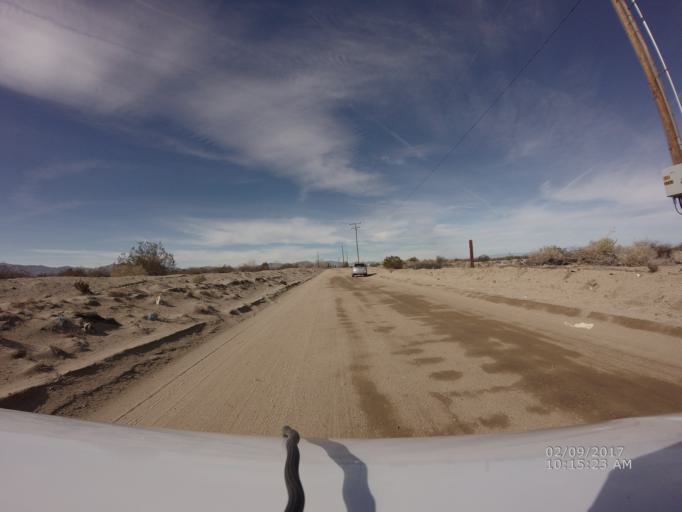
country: US
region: California
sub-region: Los Angeles County
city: Littlerock
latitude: 34.5725
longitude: -117.9138
